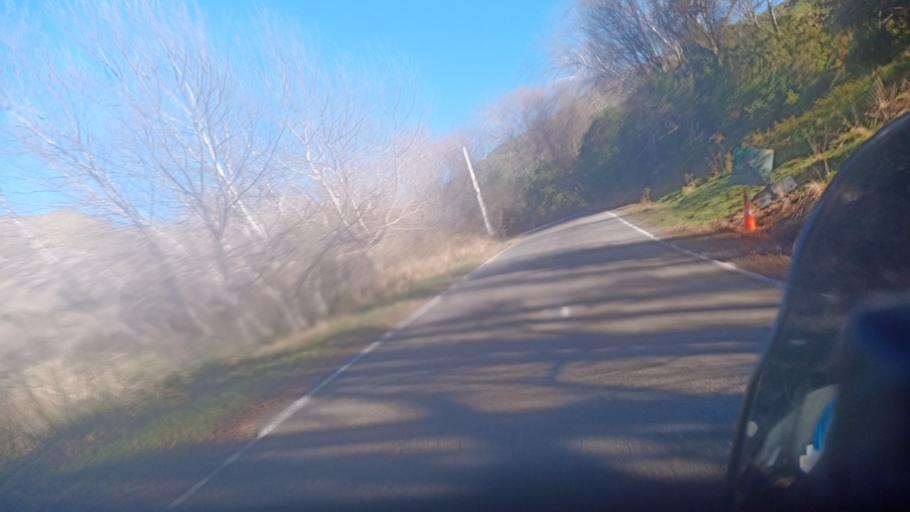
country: NZ
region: Gisborne
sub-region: Gisborne District
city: Gisborne
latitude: -38.5711
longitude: 177.5927
